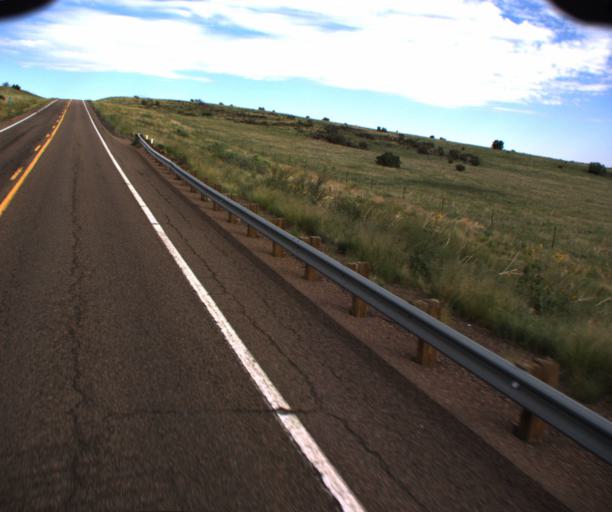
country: US
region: Arizona
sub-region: Apache County
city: Springerville
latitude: 34.2236
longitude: -109.4855
